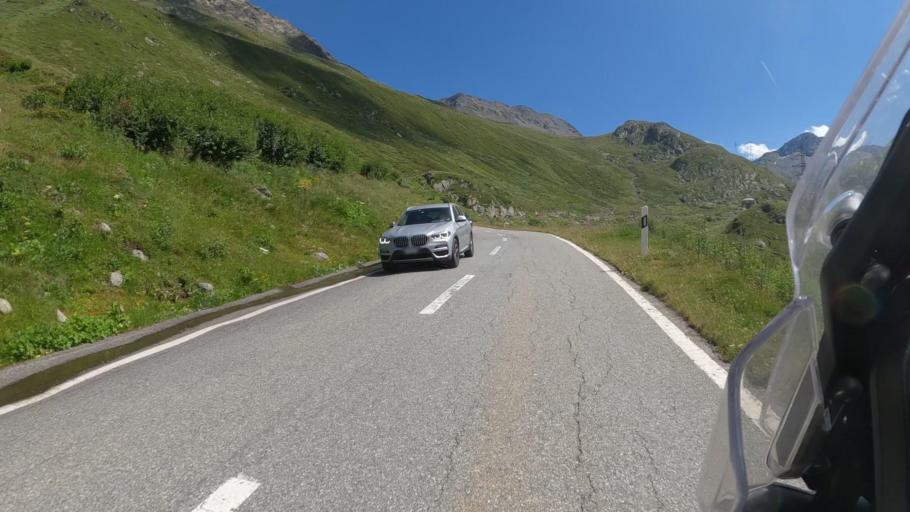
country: IT
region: Aosta Valley
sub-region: Valle d'Aosta
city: San Leonardo
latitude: 45.8907
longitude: 7.1877
